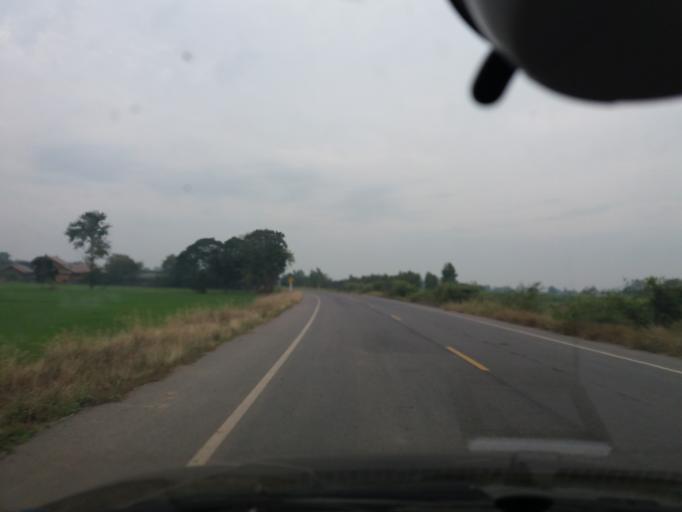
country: TH
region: Suphan Buri
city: Doem Bang Nang Buat
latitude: 14.8596
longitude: 100.1285
